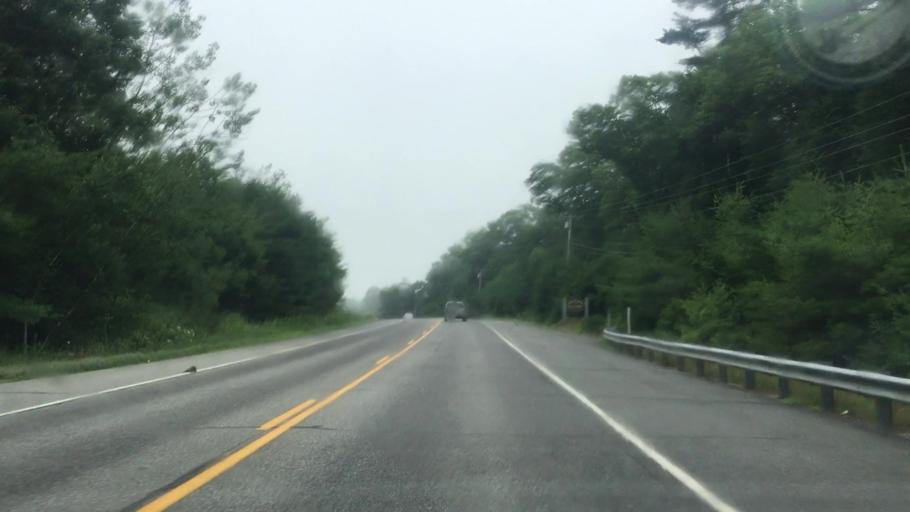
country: US
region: Maine
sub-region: Lincoln County
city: Edgecomb
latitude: 43.9398
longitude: -69.6255
